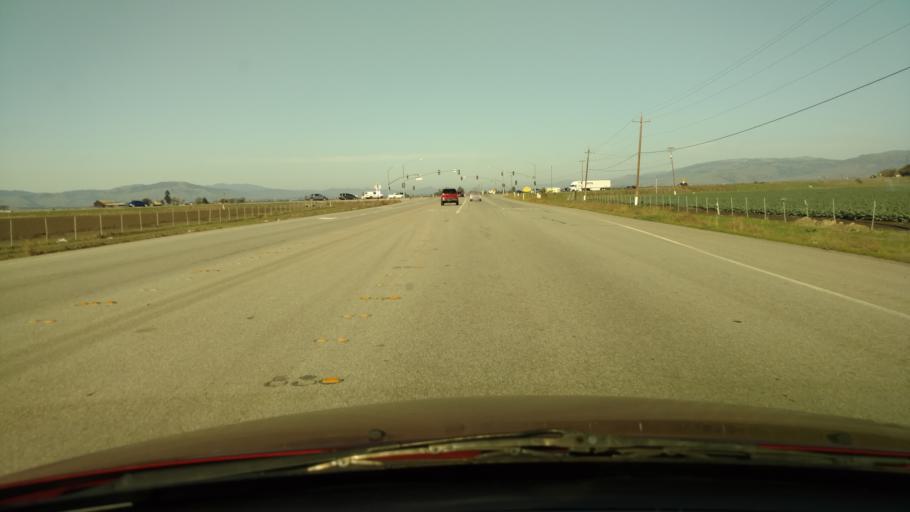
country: US
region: California
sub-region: San Benito County
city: Hollister
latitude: 36.8939
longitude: -121.4256
